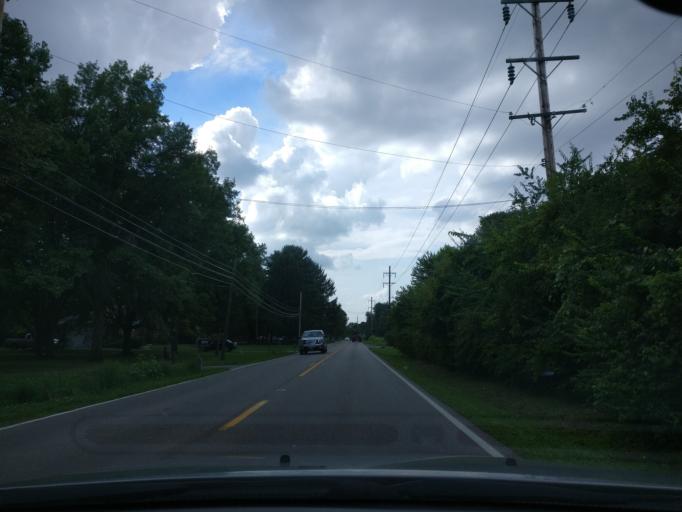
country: US
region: Ohio
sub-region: Montgomery County
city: Centerville
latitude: 39.5886
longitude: -84.1370
